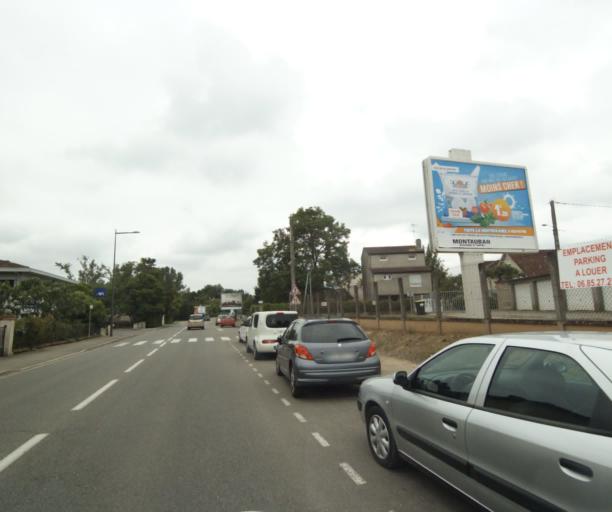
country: FR
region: Midi-Pyrenees
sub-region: Departement du Tarn-et-Garonne
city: Montauban
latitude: 44.0099
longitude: 1.3556
